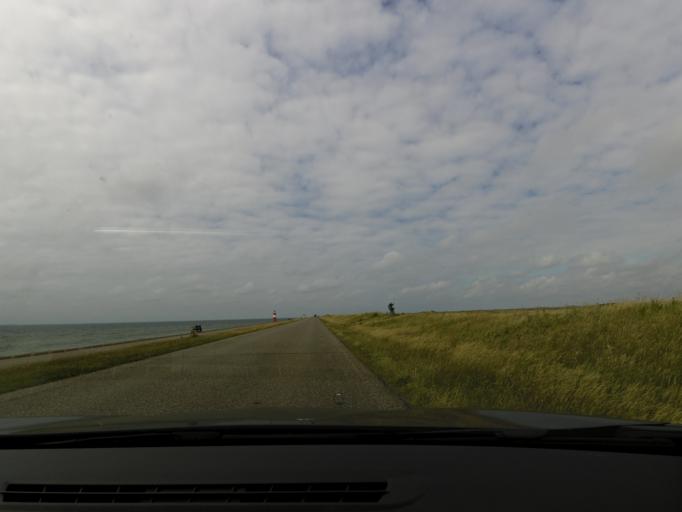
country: NL
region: Zeeland
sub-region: Gemeente Vlissingen
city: Vlissingen
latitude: 51.5362
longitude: 3.4365
